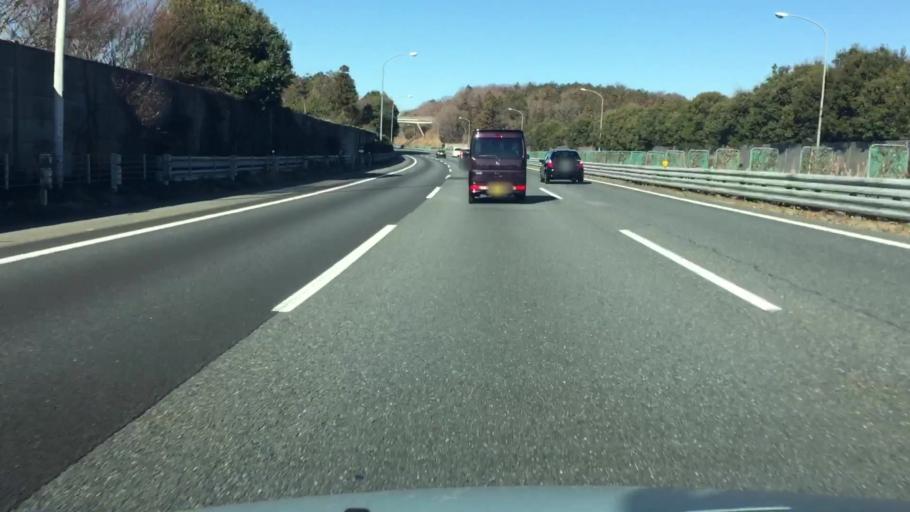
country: JP
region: Saitama
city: Ogawa
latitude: 36.0532
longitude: 139.3399
